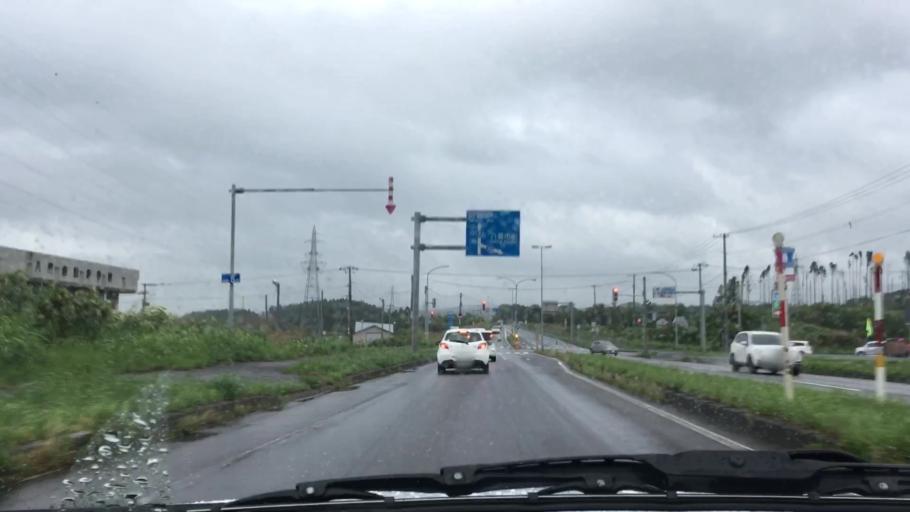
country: JP
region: Hokkaido
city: Nanae
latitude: 42.2467
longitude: 140.2891
